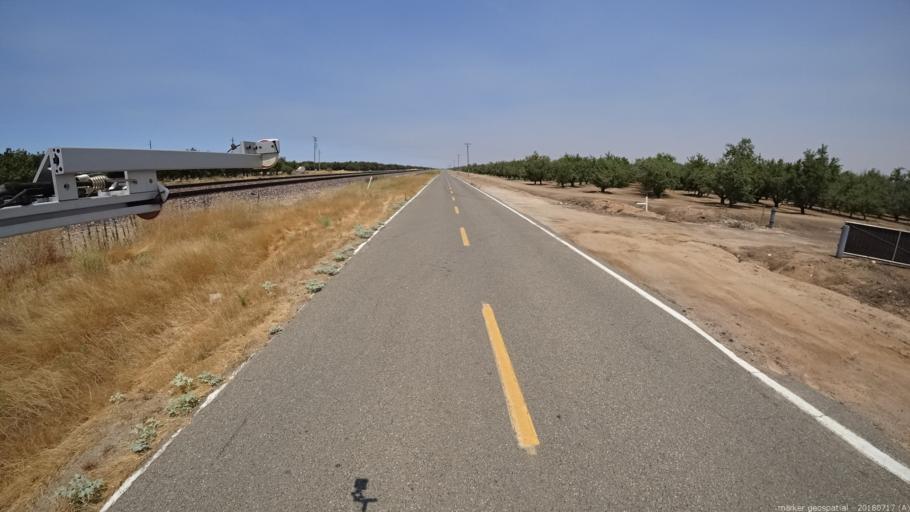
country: US
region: California
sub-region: Madera County
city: Fairmead
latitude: 37.1124
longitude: -120.1405
